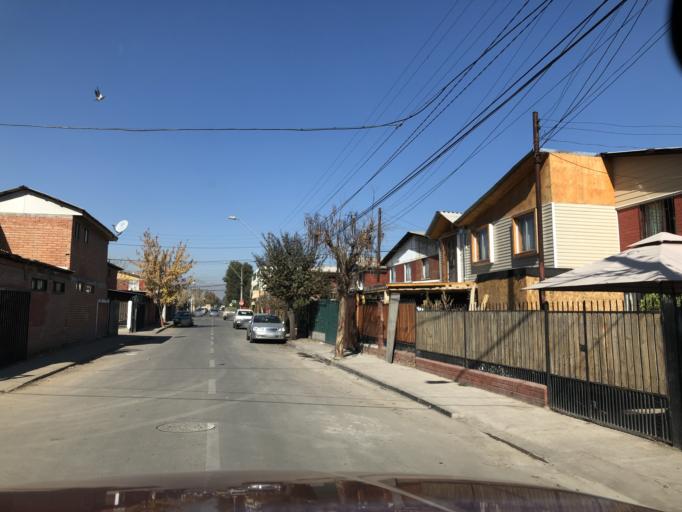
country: CL
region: Santiago Metropolitan
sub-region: Provincia de Cordillera
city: Puente Alto
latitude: -33.5641
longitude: -70.5733
